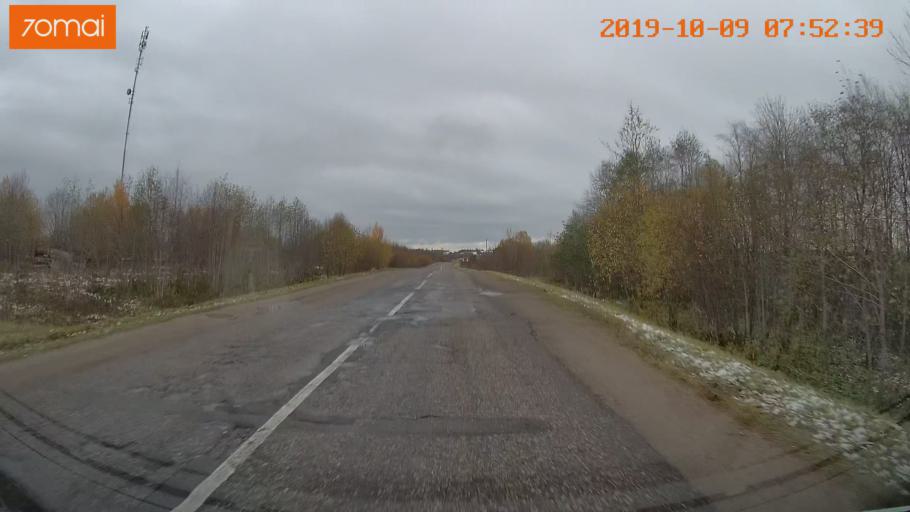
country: RU
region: Jaroslavl
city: Kukoboy
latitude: 58.6928
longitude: 39.8889
